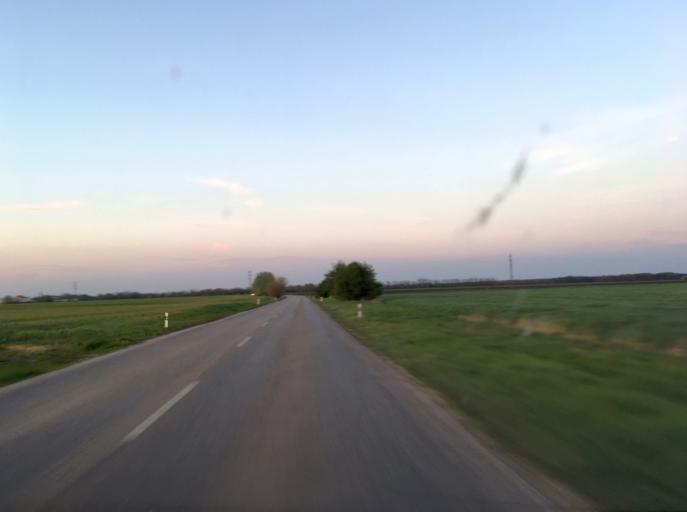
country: SK
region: Nitriansky
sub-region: Okres Nove Zamky
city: Nove Zamky
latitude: 47.9437
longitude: 18.1320
